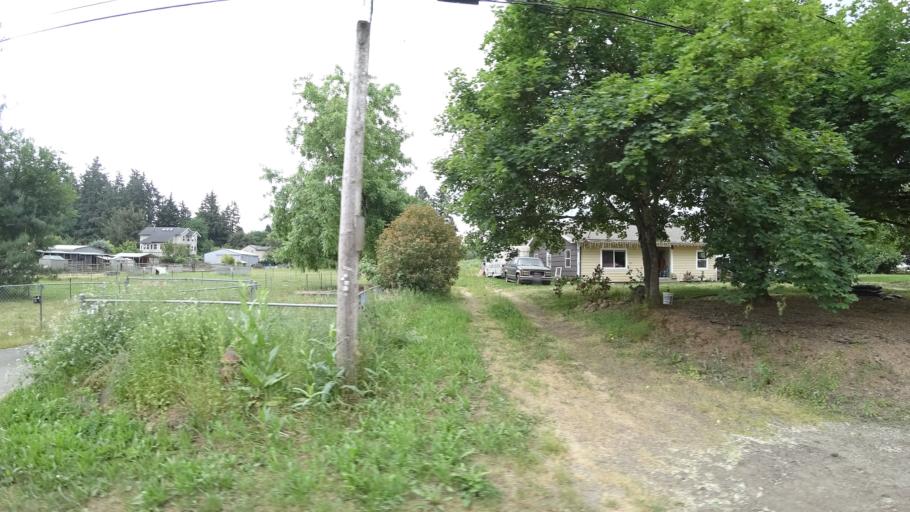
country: US
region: Oregon
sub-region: Multnomah County
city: Lents
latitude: 45.4879
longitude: -122.5298
